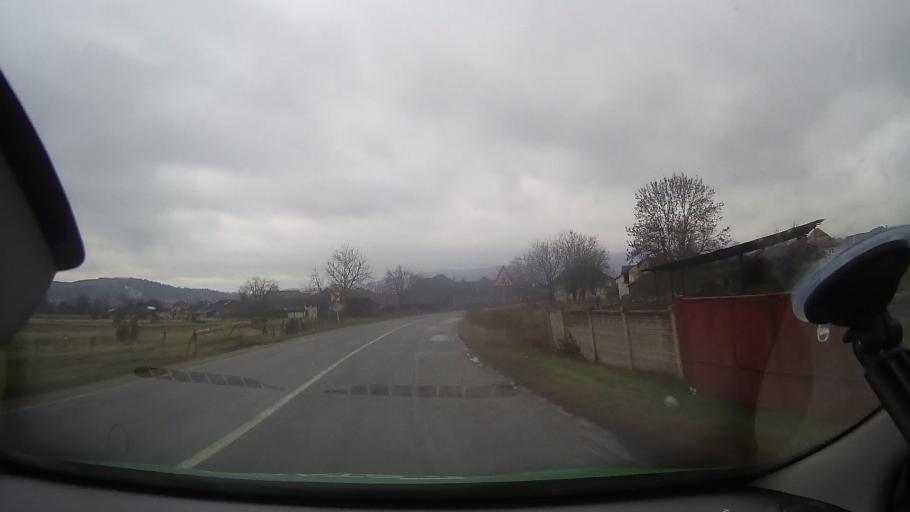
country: RO
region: Arad
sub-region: Comuna Halmagiu
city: Halmagiu
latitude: 46.2657
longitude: 22.5969
